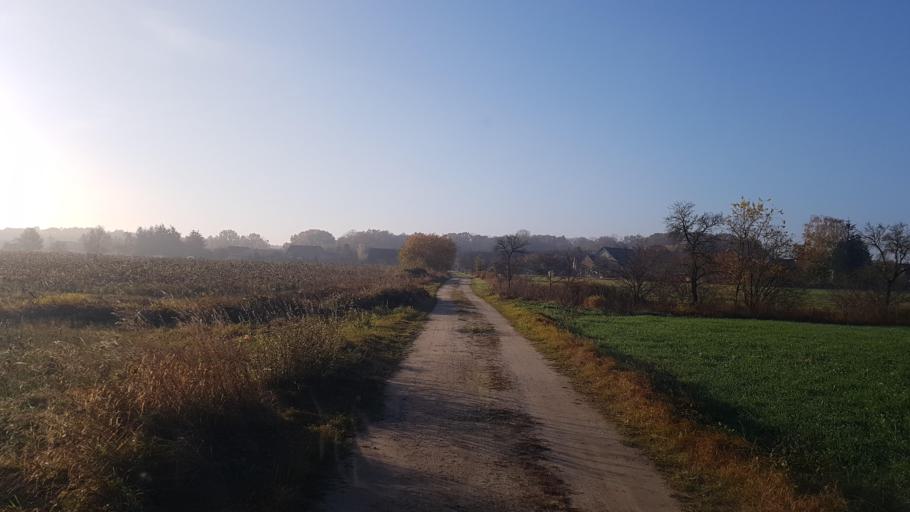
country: DE
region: Brandenburg
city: Altdobern
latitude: 51.6946
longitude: 14.0073
